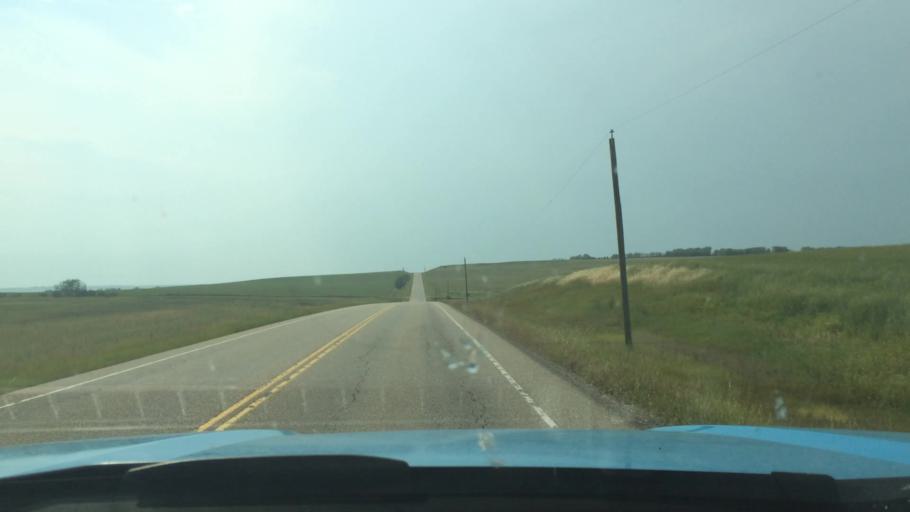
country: CA
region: Alberta
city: Airdrie
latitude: 51.2125
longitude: -114.1106
